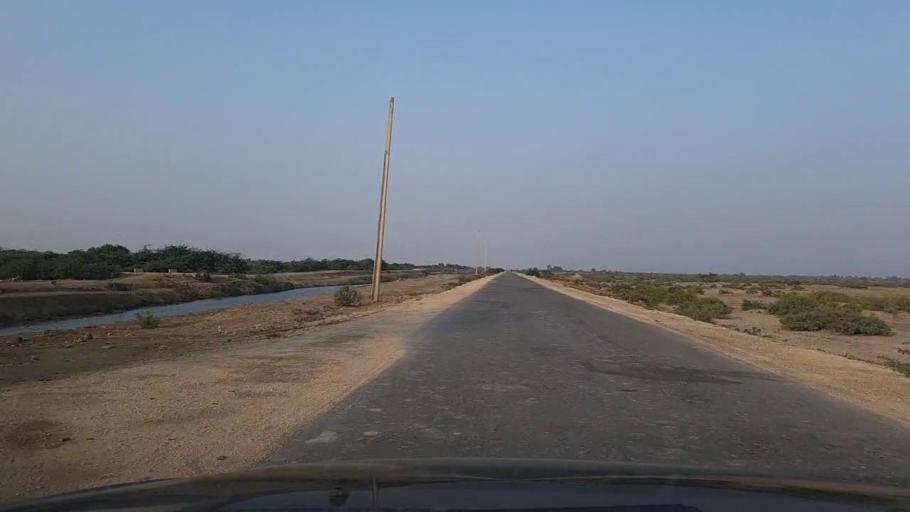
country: PK
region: Sindh
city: Mirpur Sakro
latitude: 24.4696
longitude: 67.7997
